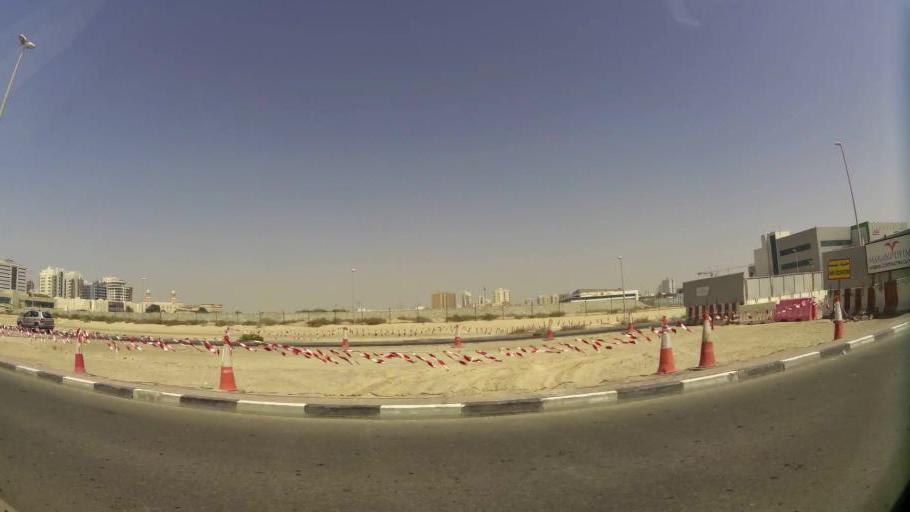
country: AE
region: Ash Shariqah
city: Sharjah
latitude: 25.2854
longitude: 55.3645
